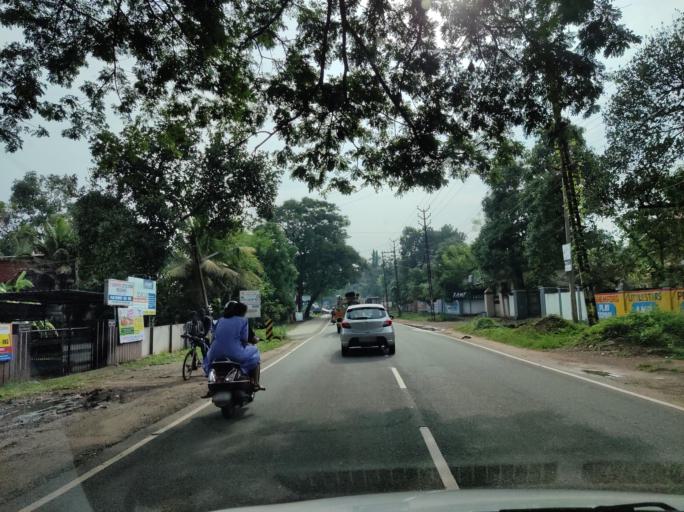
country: IN
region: Kerala
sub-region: Alappuzha
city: Kattanam
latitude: 9.1723
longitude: 76.6044
